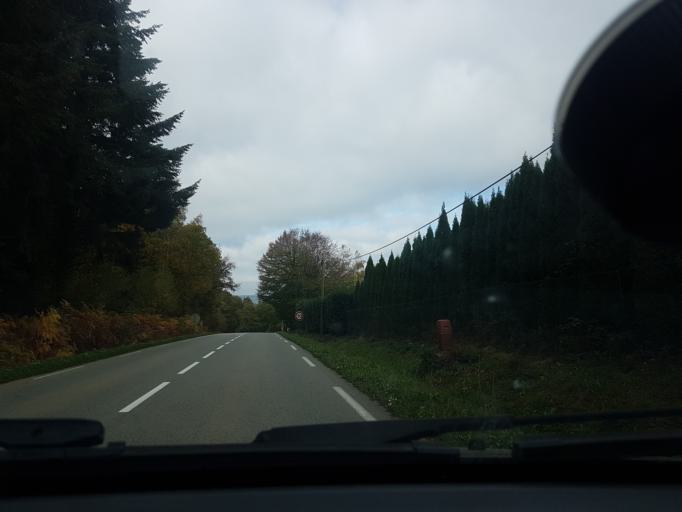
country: FR
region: Franche-Comte
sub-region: Departement de la Haute-Saone
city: Plancher-Bas
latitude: 47.6967
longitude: 6.7356
